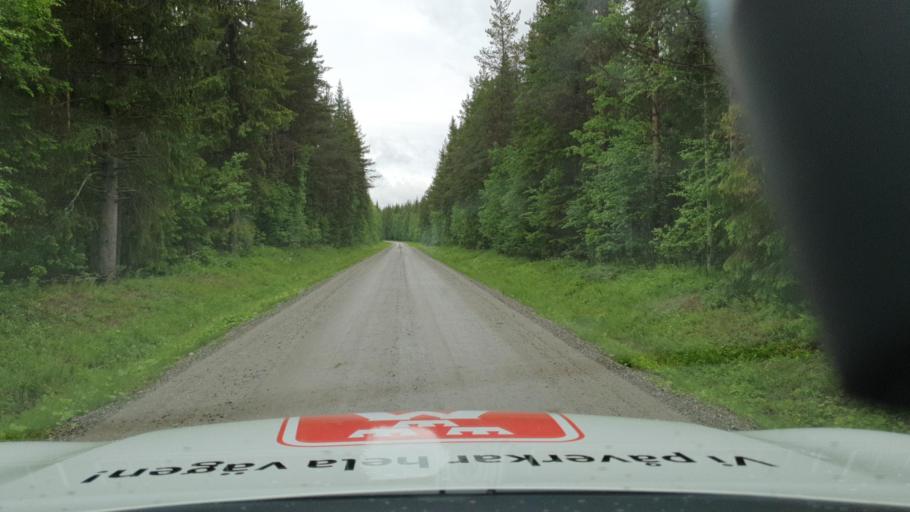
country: SE
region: Vaesterbotten
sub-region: Dorotea Kommun
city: Dorotea
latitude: 64.0746
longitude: 16.6925
